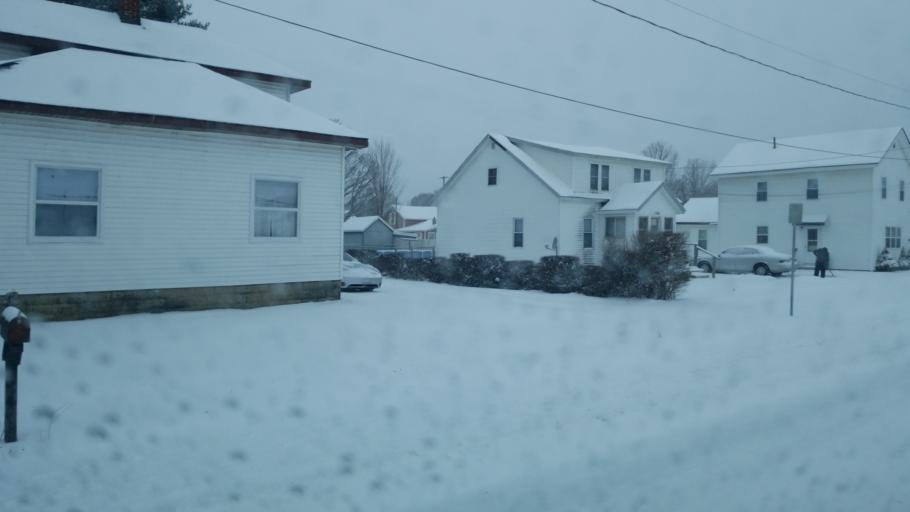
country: US
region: Michigan
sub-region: Osceola County
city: Evart
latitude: 43.8996
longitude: -85.2607
